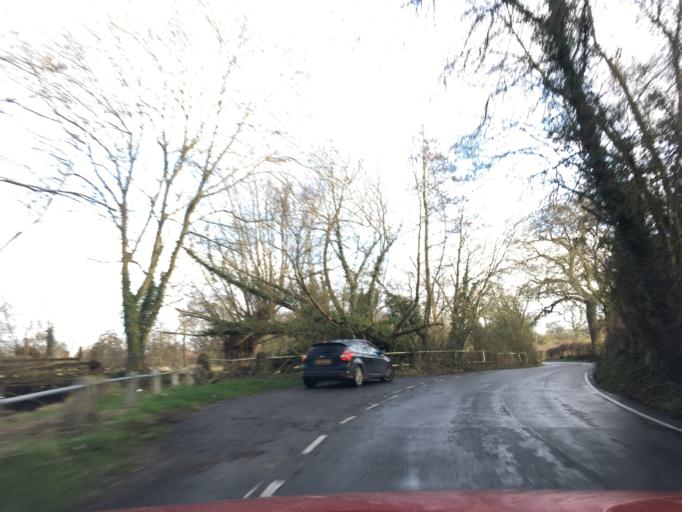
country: GB
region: England
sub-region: Warwickshire
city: Alcester
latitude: 52.2258
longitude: -1.8216
